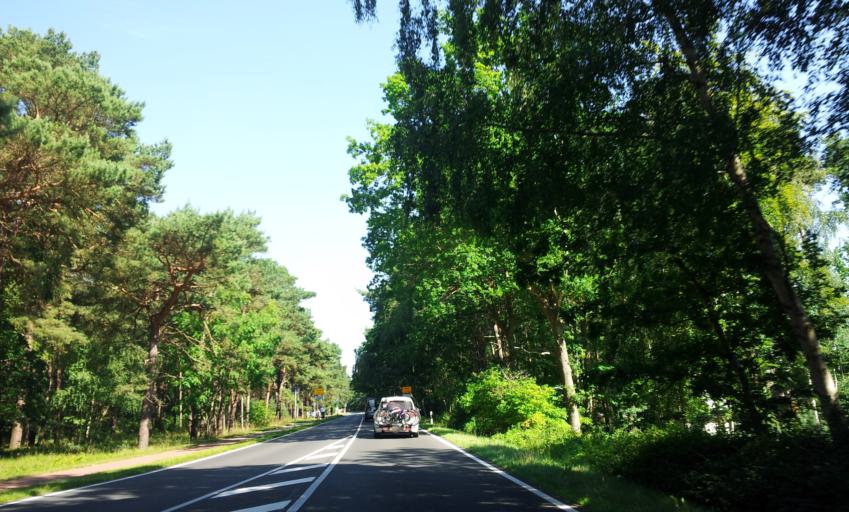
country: DE
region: Mecklenburg-Vorpommern
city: Glowe
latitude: 54.5697
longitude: 13.4505
